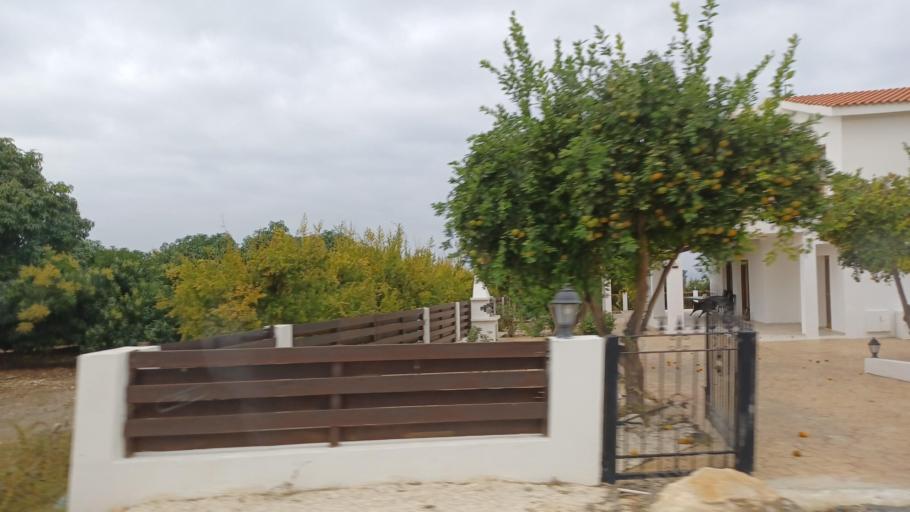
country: CY
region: Pafos
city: Pegeia
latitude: 34.8967
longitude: 32.3350
